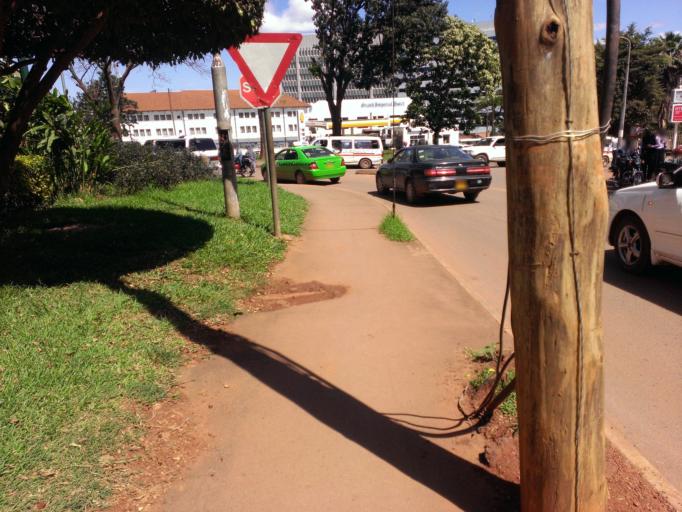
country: UG
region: Central Region
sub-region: Kampala District
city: Kampala
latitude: 0.3164
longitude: 32.5804
